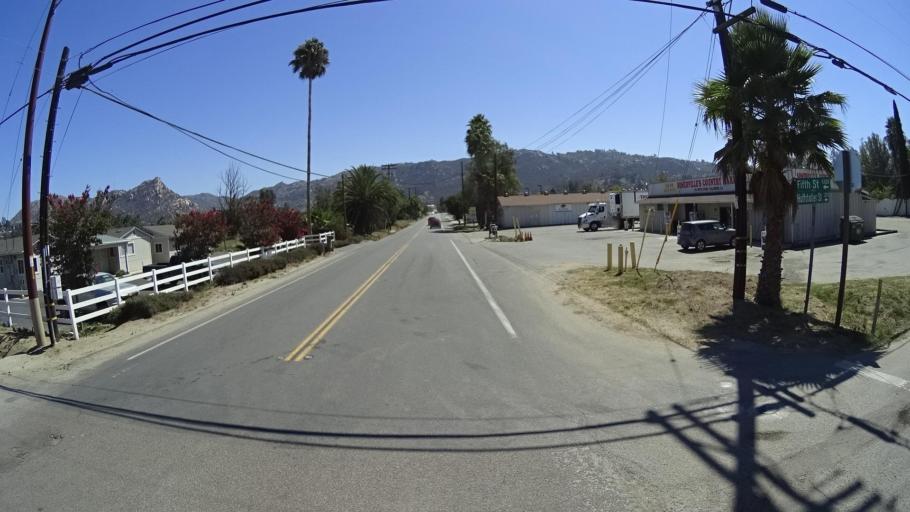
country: US
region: California
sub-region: San Diego County
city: Rainbow
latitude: 33.4139
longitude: -117.1520
